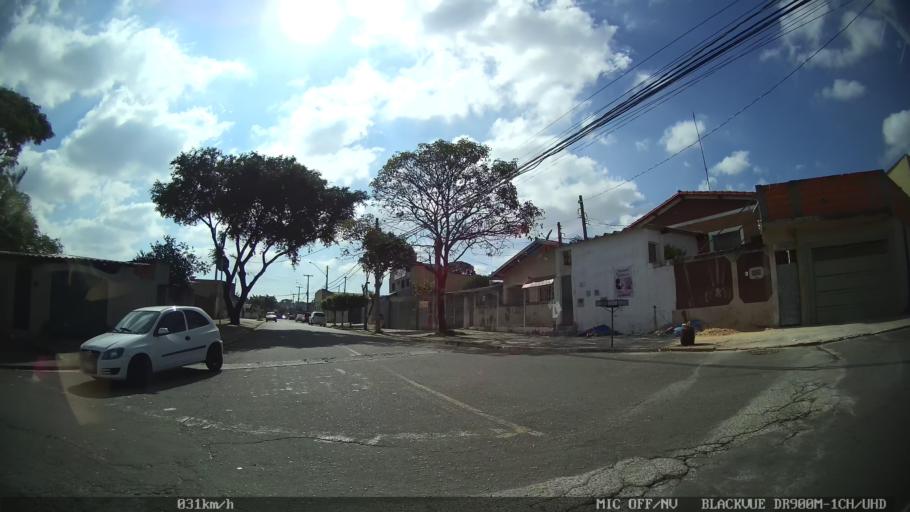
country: BR
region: Sao Paulo
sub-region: Campinas
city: Campinas
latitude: -22.9387
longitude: -47.1078
